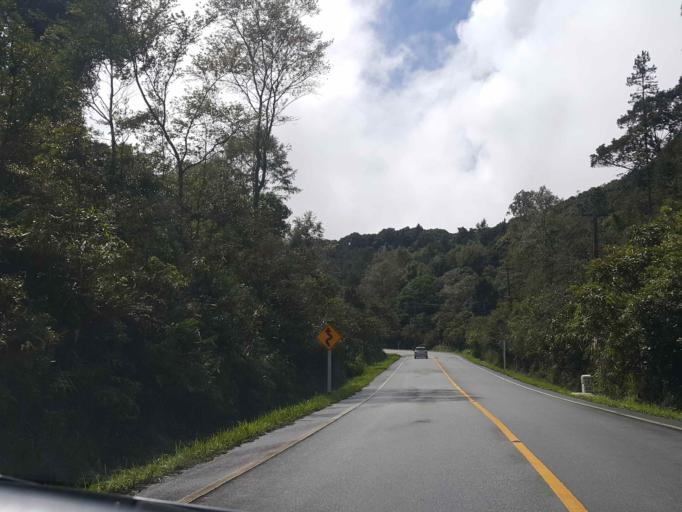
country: TH
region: Chiang Mai
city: Mae Chaem
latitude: 18.5119
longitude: 98.5091
